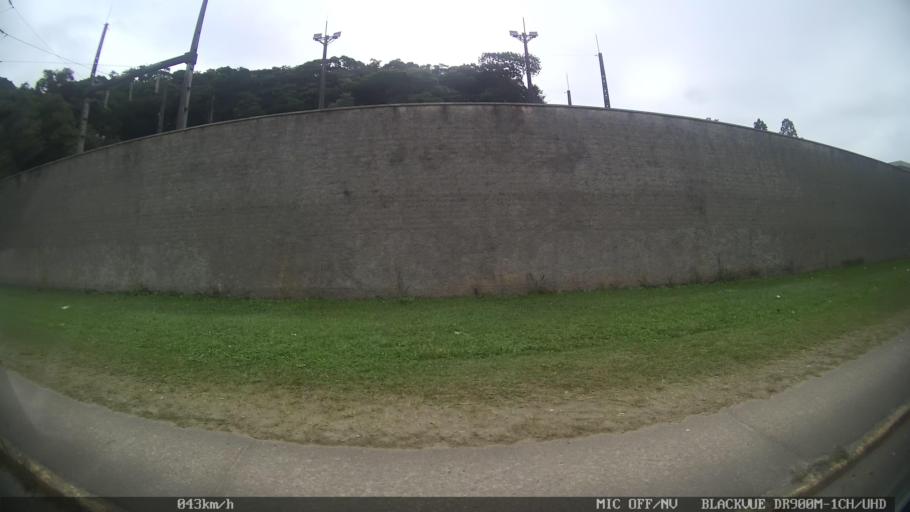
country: BR
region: Santa Catarina
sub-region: Joinville
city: Joinville
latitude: -26.2615
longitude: -48.8569
